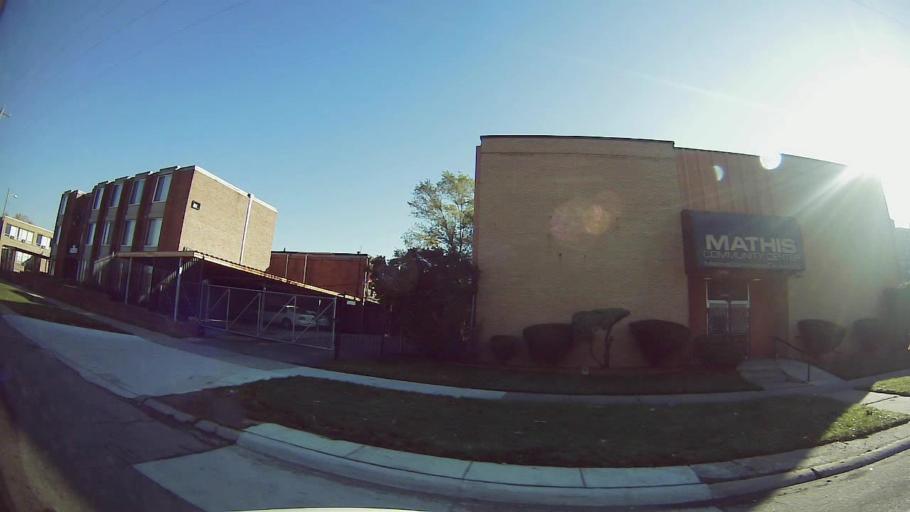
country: US
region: Michigan
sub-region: Oakland County
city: Oak Park
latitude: 42.4324
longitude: -83.1999
